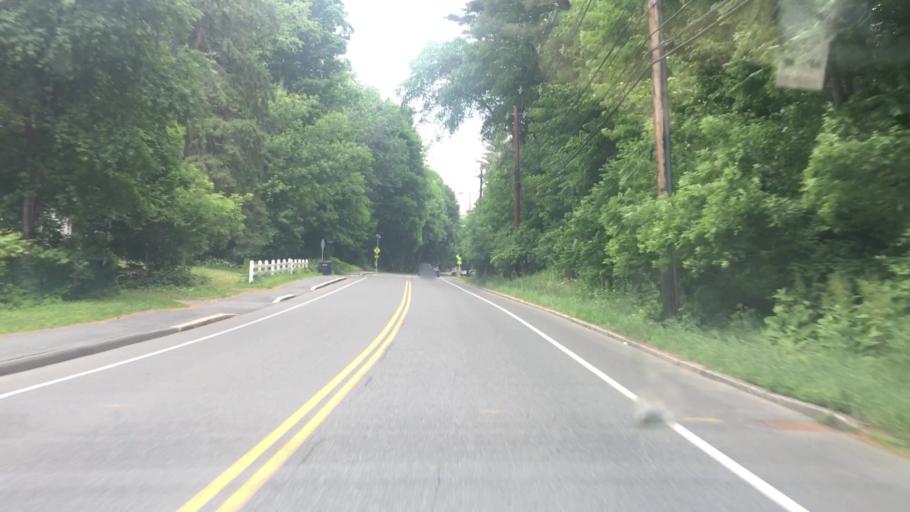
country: US
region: New Hampshire
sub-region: Grafton County
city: Hanover
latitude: 43.6961
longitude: -72.2898
